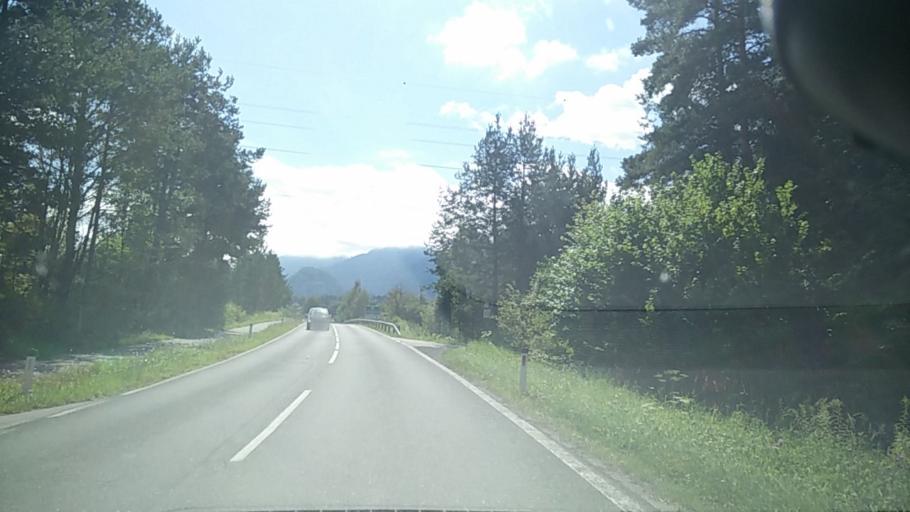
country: AT
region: Carinthia
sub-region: Politischer Bezirk Villach Land
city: Finkenstein am Faaker See
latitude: 46.5721
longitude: 13.8405
